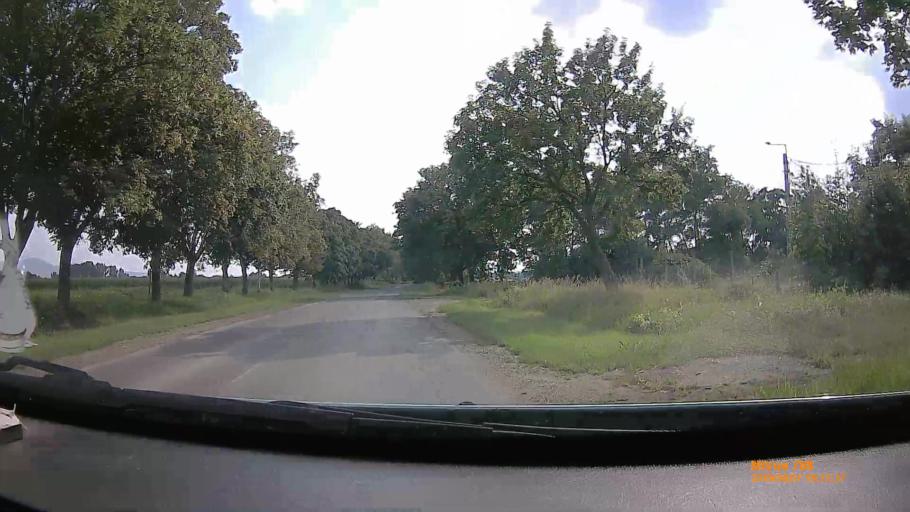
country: HU
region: Borsod-Abauj-Zemplen
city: Gonc
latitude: 48.4684
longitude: 21.2543
